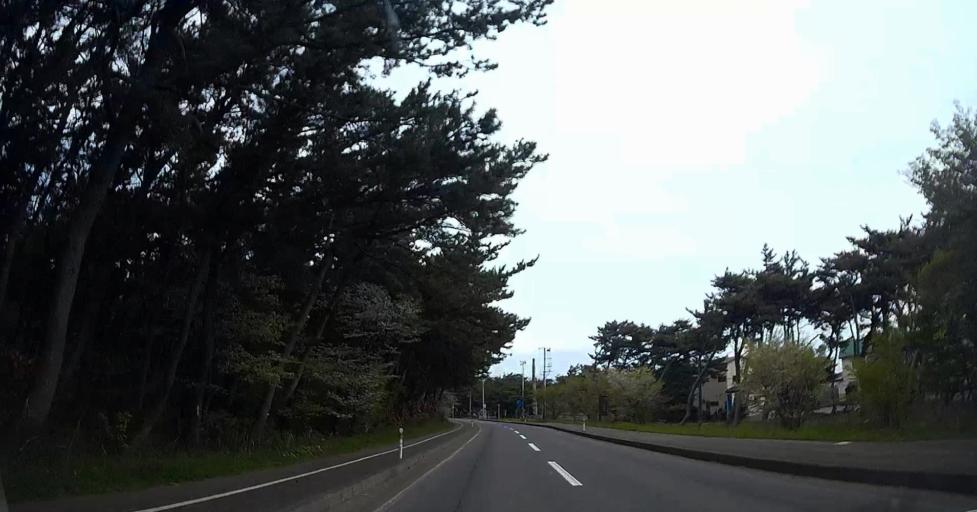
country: JP
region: Aomori
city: Shimokizukuri
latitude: 41.0423
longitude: 140.3265
